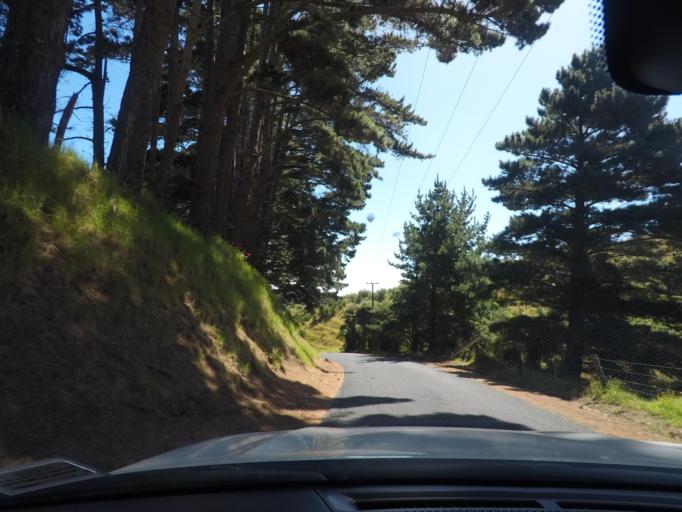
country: NZ
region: Auckland
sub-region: Auckland
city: Parakai
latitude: -36.5894
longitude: 174.2883
